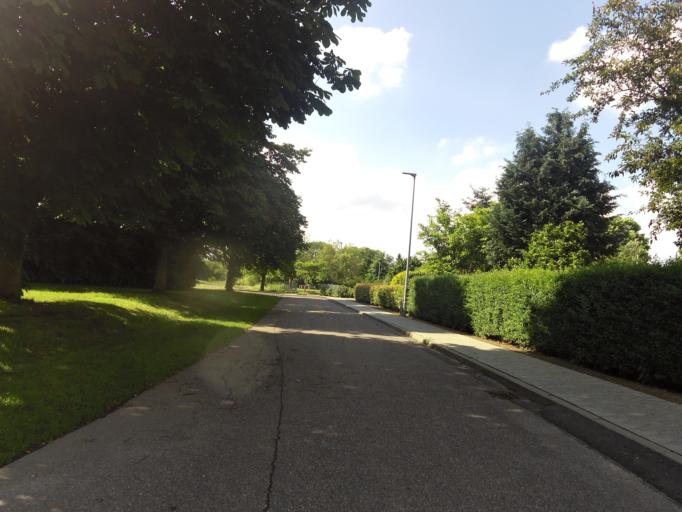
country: DK
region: South Denmark
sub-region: Vejen Kommune
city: Rodding
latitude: 55.3652
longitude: 9.0652
